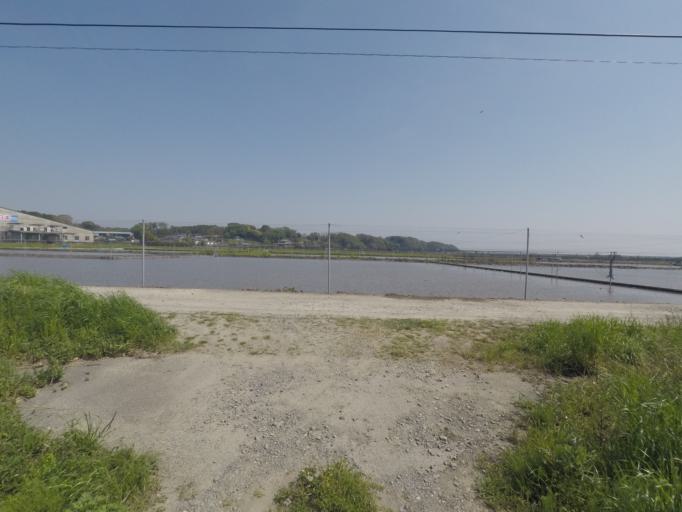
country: JP
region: Ibaraki
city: Ami
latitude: 36.0898
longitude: 140.2379
